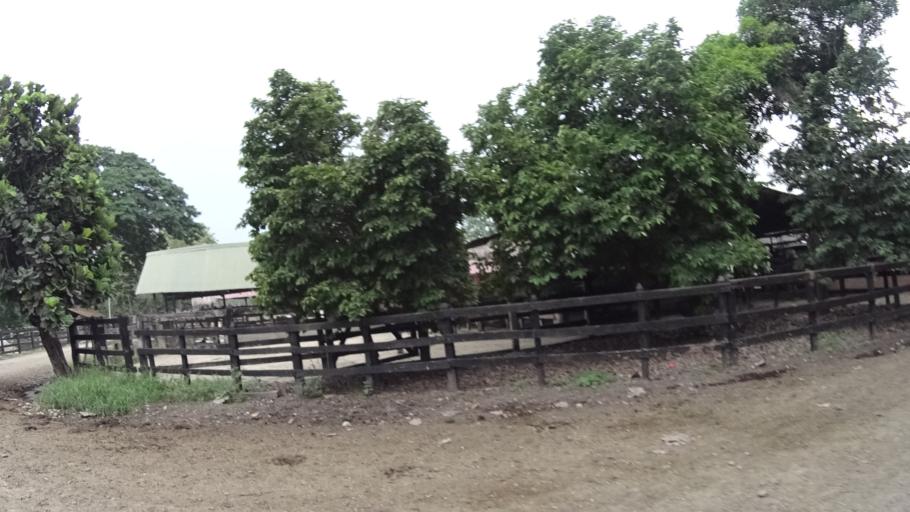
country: CO
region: Cundinamarca
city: Puerto Salgar
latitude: 5.4833
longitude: -74.7068
